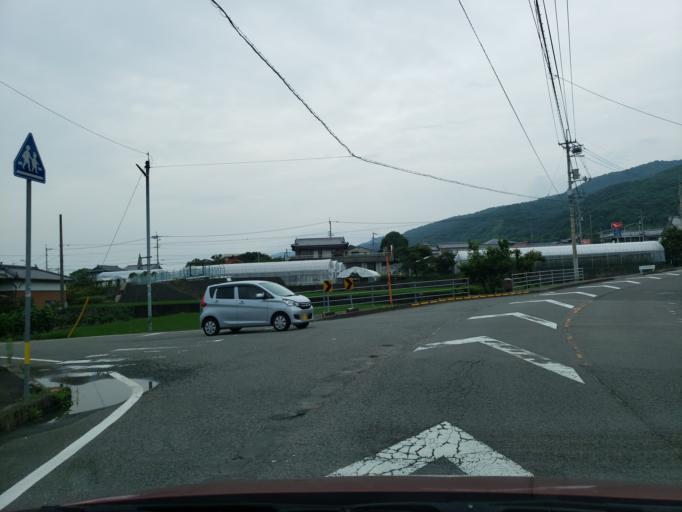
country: JP
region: Tokushima
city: Kamojimacho-jogejima
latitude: 34.1040
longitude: 134.2659
